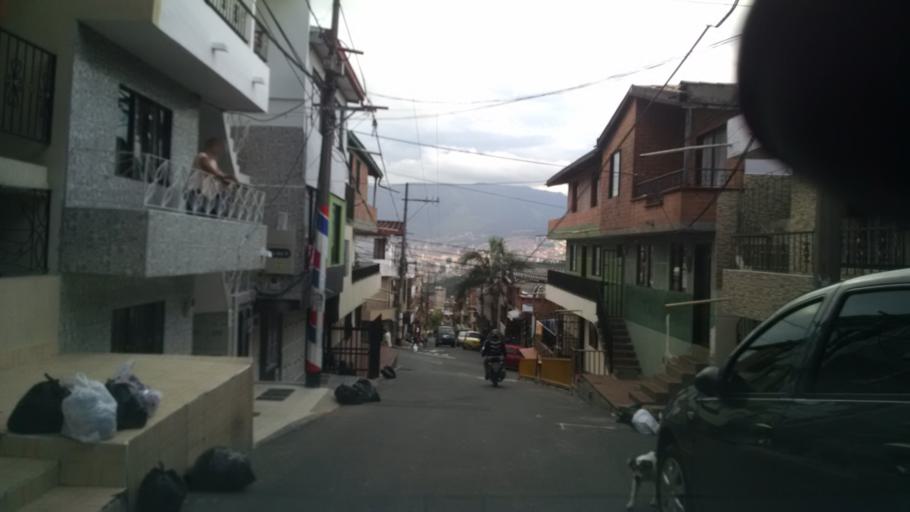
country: CO
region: Antioquia
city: Medellin
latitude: 6.2830
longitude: -75.5904
